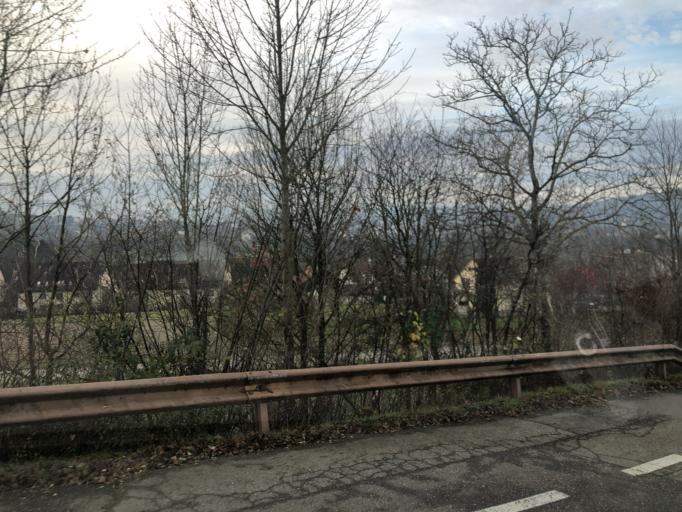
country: CH
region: Aargau
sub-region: Bezirk Baden
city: Gebenstorf
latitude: 47.4769
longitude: 8.2338
